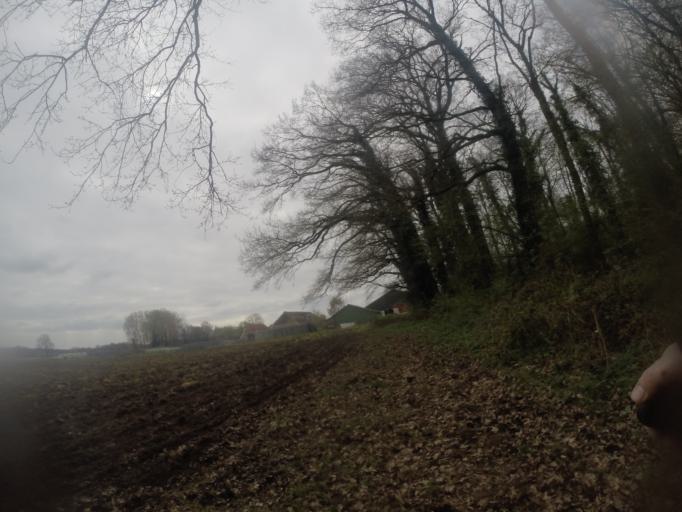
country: NL
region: Gelderland
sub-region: Gemeente Zutphen
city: Leesten
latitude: 52.1184
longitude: 6.2724
